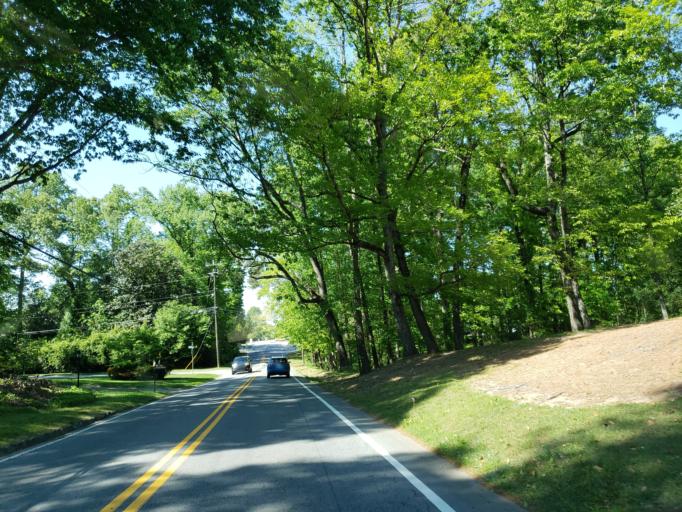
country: US
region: Georgia
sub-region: Fulton County
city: Sandy Springs
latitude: 33.9132
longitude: -84.4066
